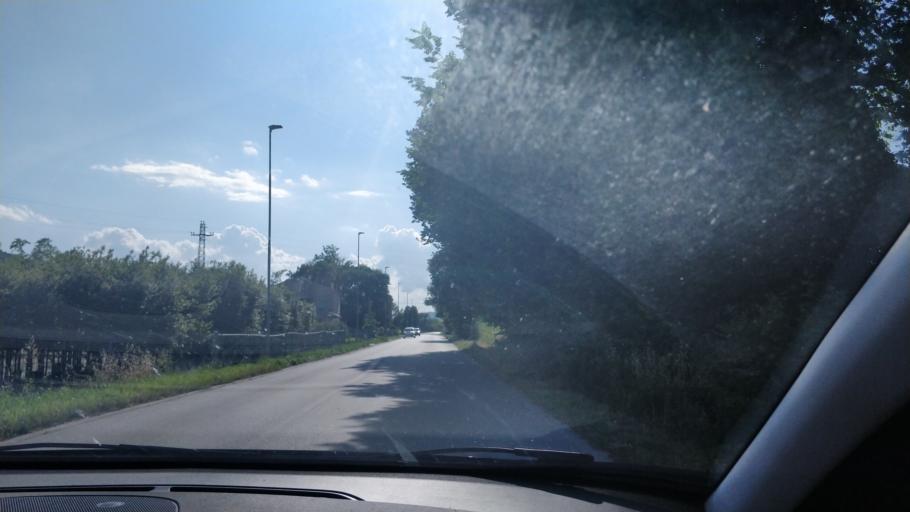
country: IT
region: The Marches
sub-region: Provincia di Ascoli Piceno
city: Massignano
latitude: 43.0363
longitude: 13.8228
